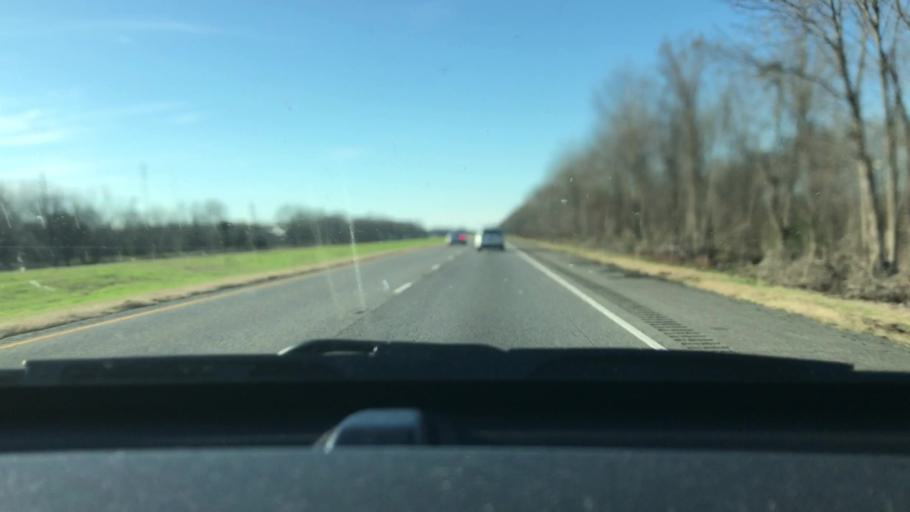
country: US
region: Louisiana
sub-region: Rapides Parish
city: Boyce
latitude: 31.3751
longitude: -92.6366
